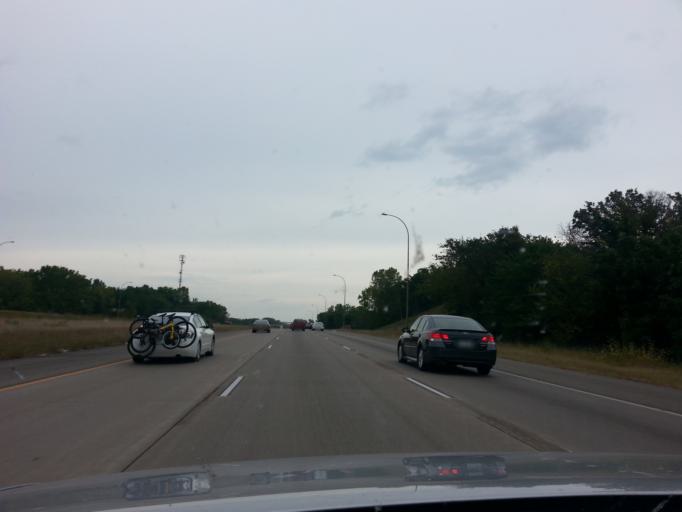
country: US
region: Minnesota
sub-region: Washington County
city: Woodbury
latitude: 44.9061
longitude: -92.9899
